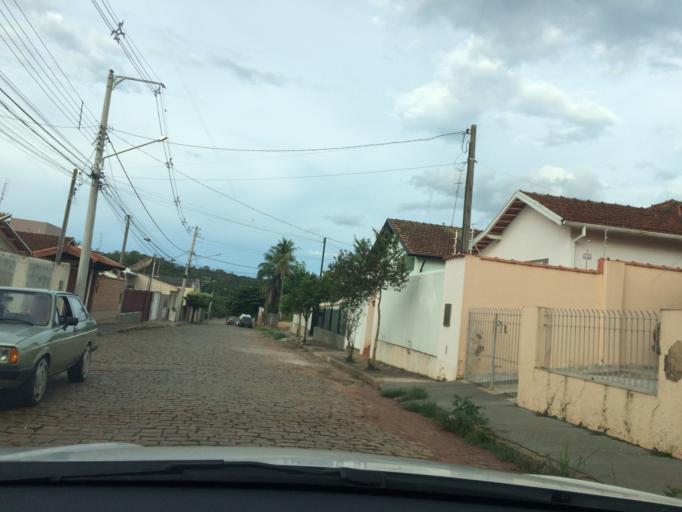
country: BR
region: Sao Paulo
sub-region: Casa Branca
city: Casa Branca
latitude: -21.7770
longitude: -47.0784
